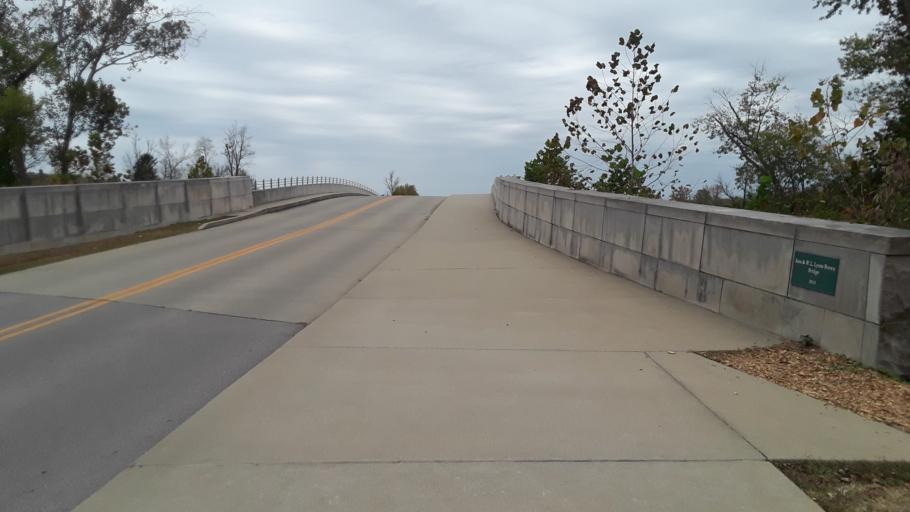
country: US
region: Kentucky
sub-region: Jefferson County
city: Middletown
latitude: 38.2070
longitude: -85.4745
